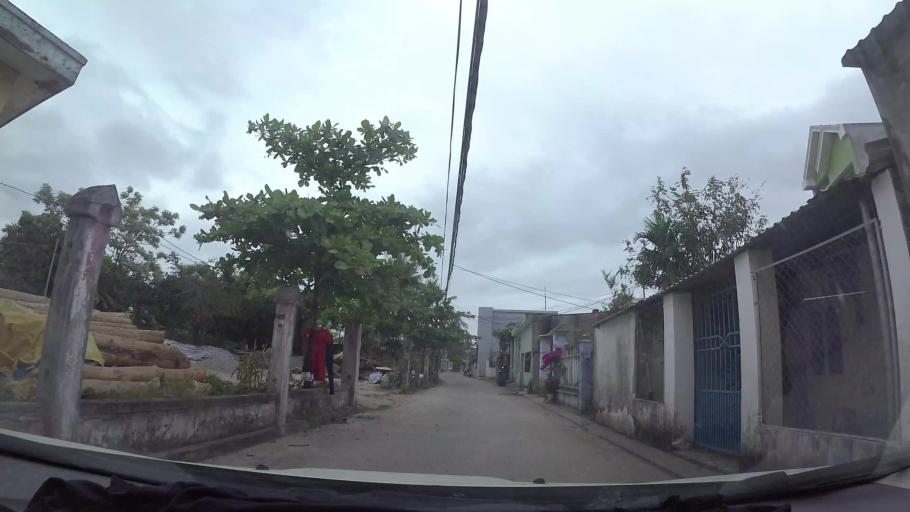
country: VN
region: Da Nang
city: Lien Chieu
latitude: 16.1041
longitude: 108.1303
